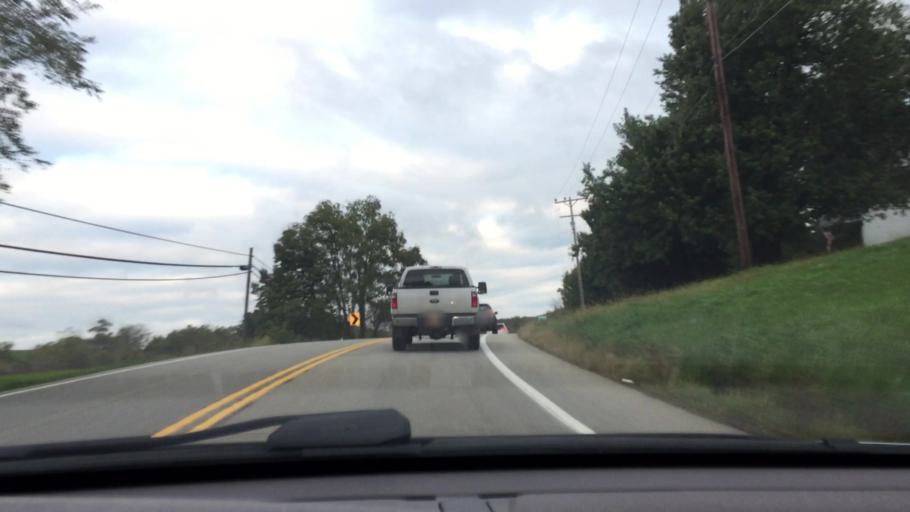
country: US
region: Pennsylvania
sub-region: Washington County
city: Canonsburg
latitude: 40.2284
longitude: -80.1645
